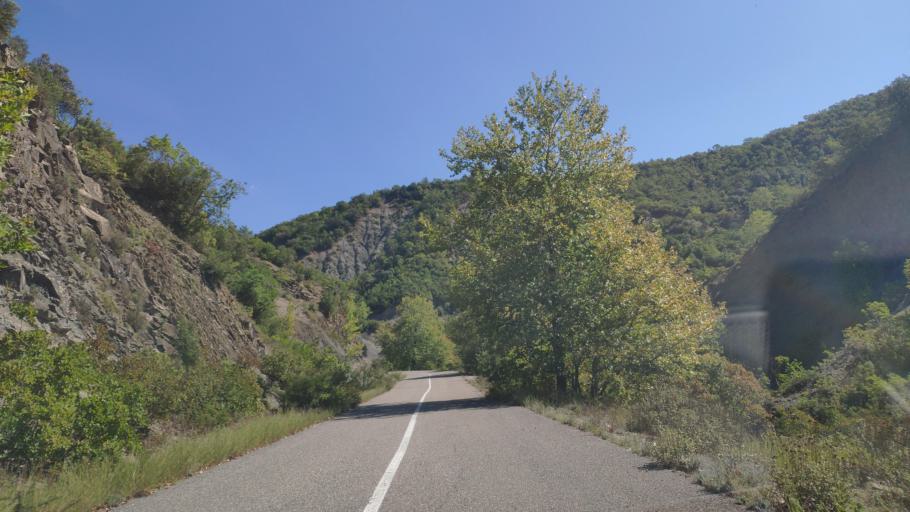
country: GR
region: Central Greece
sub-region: Nomos Evrytanias
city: Kerasochori
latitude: 39.0068
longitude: 21.5319
